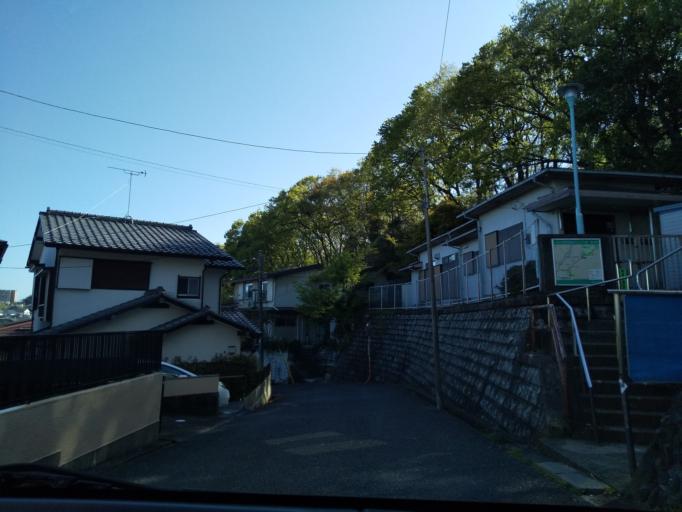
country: JP
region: Tokyo
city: Hino
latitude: 35.6521
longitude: 139.4056
